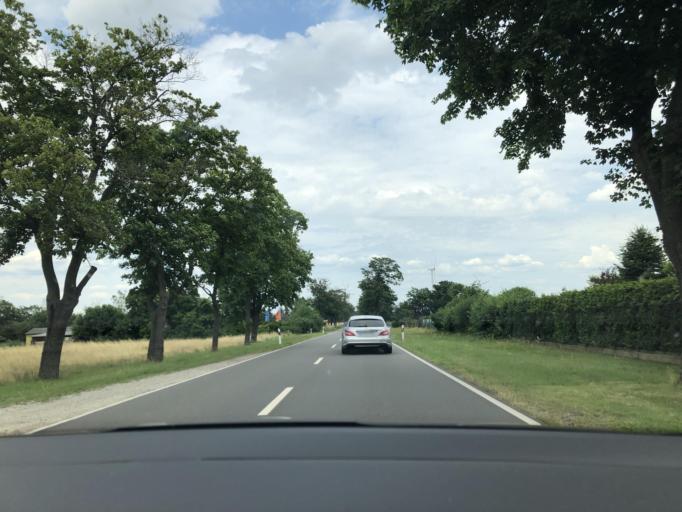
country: DE
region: Saxony-Anhalt
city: Zerbst
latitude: 51.9787
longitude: 12.1036
